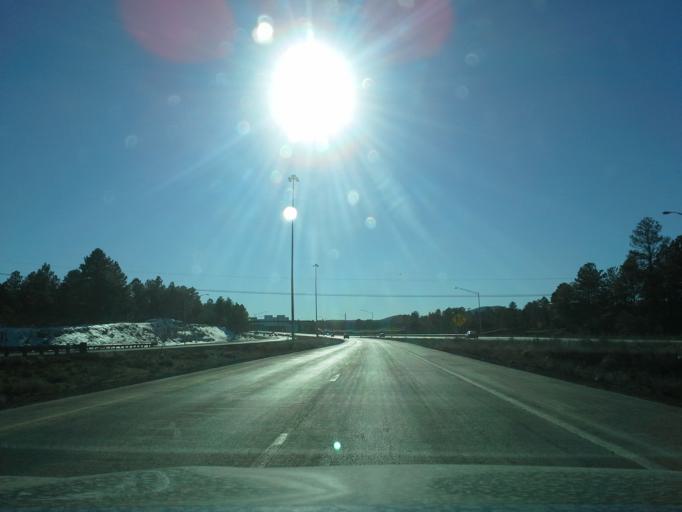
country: US
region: Arizona
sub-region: Coconino County
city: Flagstaff
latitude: 35.1687
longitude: -111.6664
